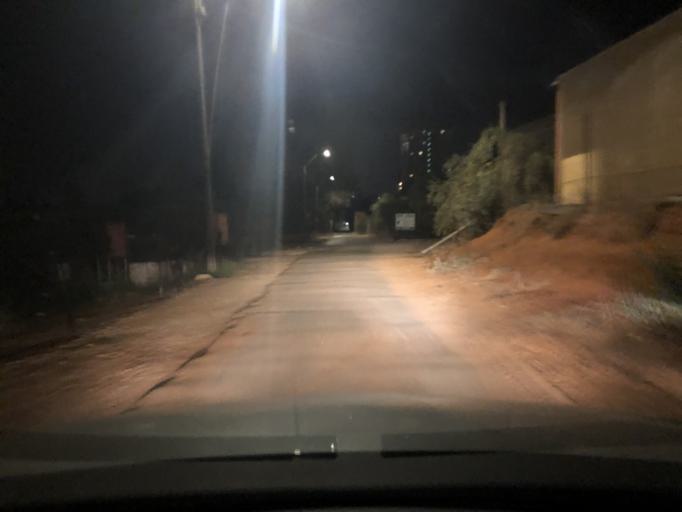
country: IL
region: Central District
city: Hod HaSharon
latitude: 32.1642
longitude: 34.8963
